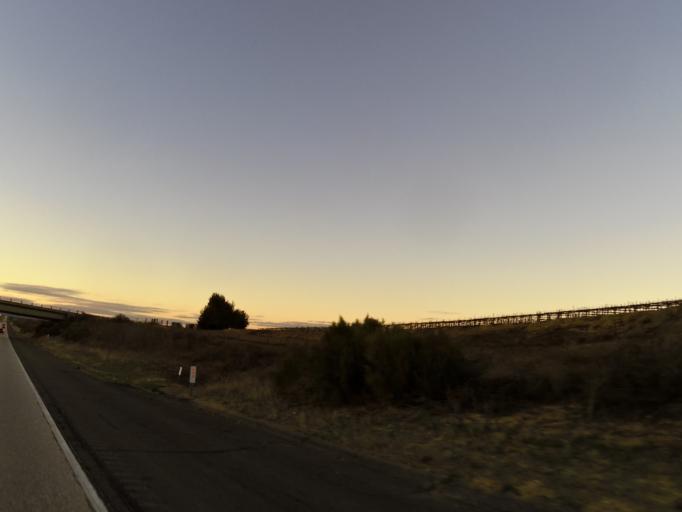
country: US
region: California
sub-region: Monterey County
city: King City
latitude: 36.0764
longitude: -120.9970
